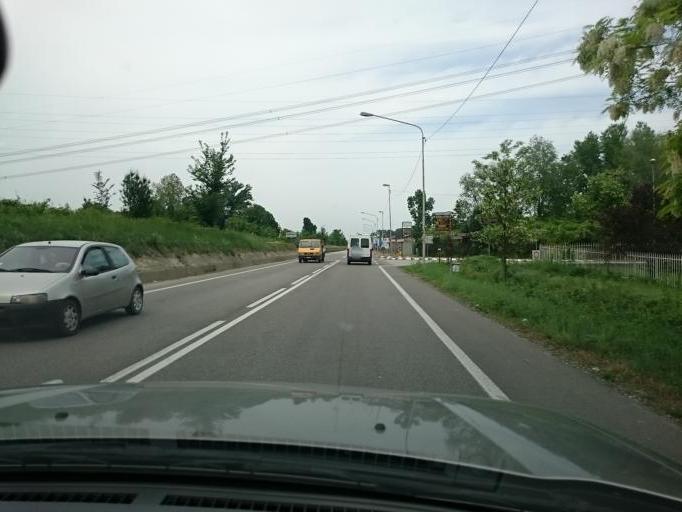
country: IT
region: Veneto
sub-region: Provincia di Padova
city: Mandriola-Sant'Agostino
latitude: 45.3595
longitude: 11.8389
